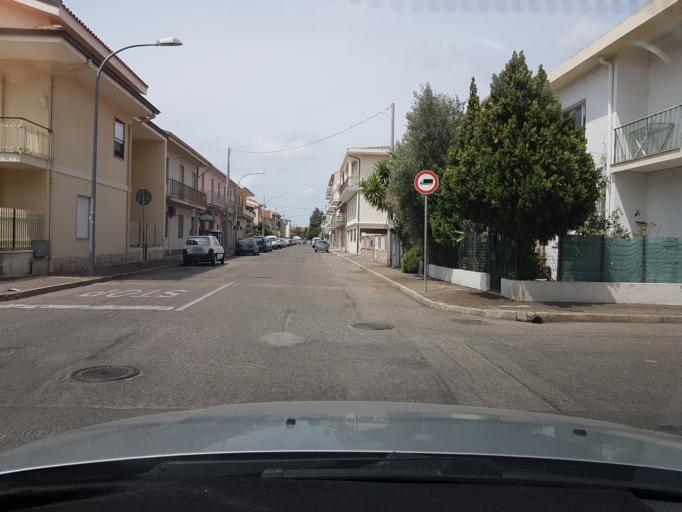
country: IT
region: Sardinia
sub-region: Provincia di Oristano
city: Oristano
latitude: 39.9105
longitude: 8.5945
